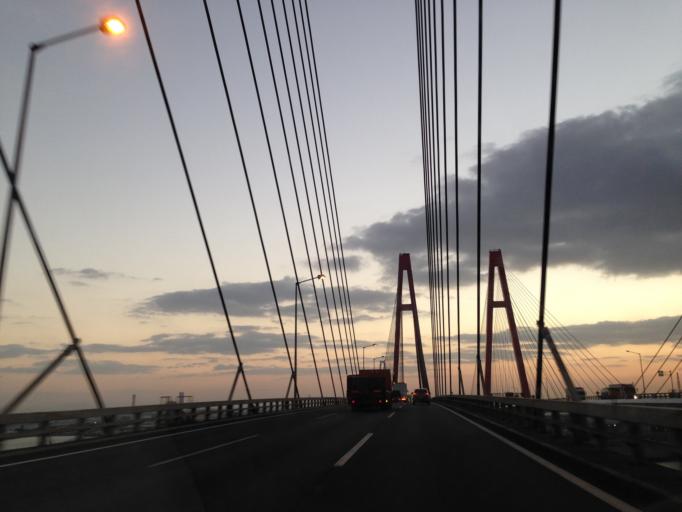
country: JP
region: Aichi
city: Kanie
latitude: 35.0520
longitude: 136.8324
